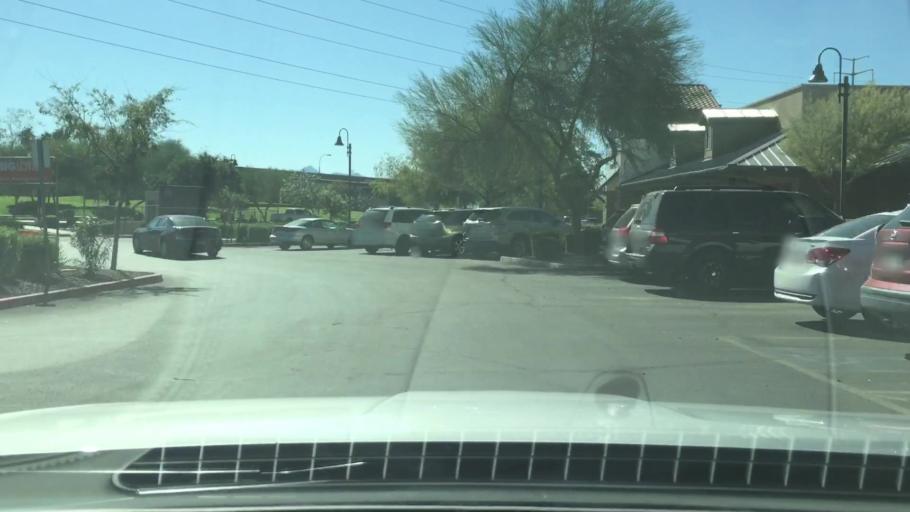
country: US
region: Arizona
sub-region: Maricopa County
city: Laveen
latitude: 33.3785
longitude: -112.1372
